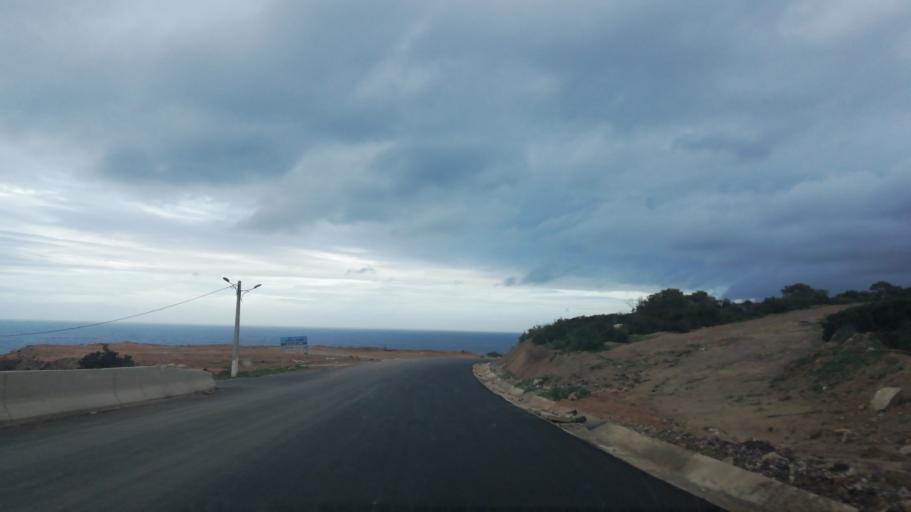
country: DZ
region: Oran
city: Bir el Djir
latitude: 35.7767
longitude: -0.5133
